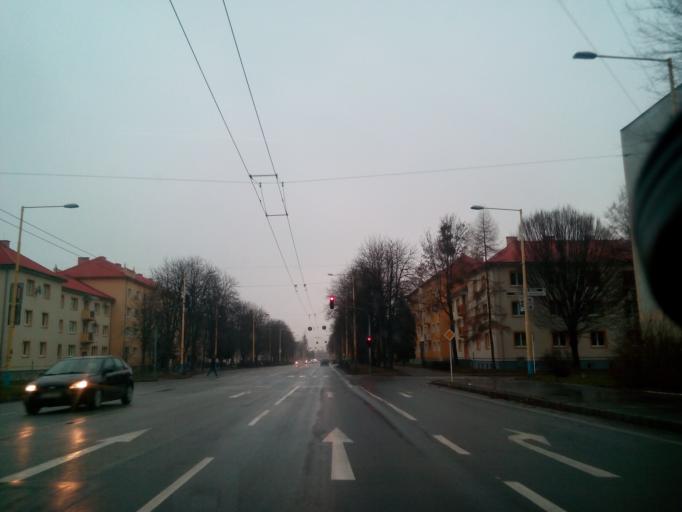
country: SK
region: Presovsky
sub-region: Okres Presov
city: Presov
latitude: 48.9987
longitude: 21.2275
